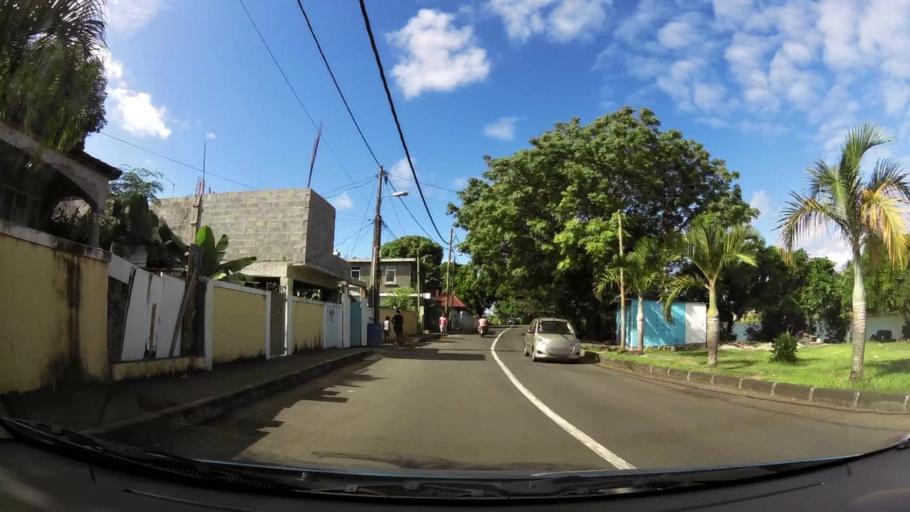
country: MU
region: Grand Port
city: Mahebourg
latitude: -20.4207
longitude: 57.7144
